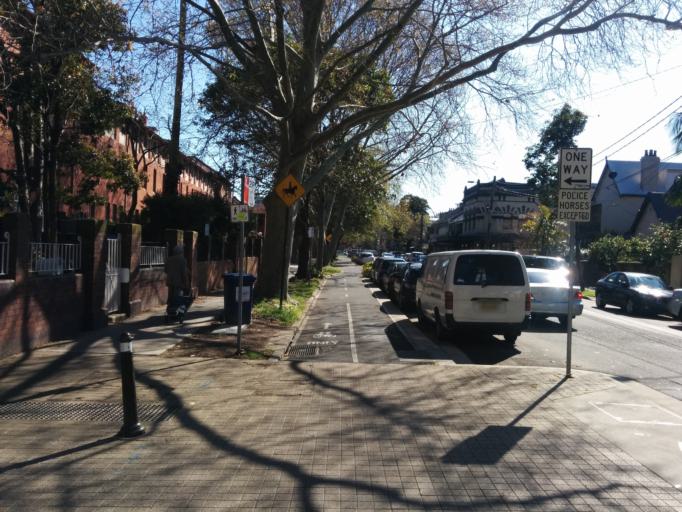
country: AU
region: New South Wales
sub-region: City of Sydney
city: Redfern
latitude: -33.8933
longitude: 151.2140
